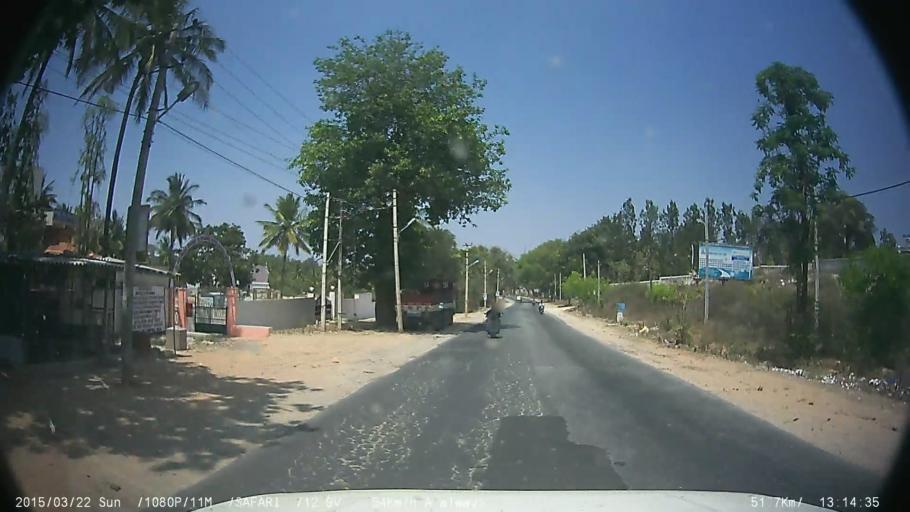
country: IN
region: Karnataka
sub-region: Bangalore Urban
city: Anekal
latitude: 12.8172
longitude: 77.5837
